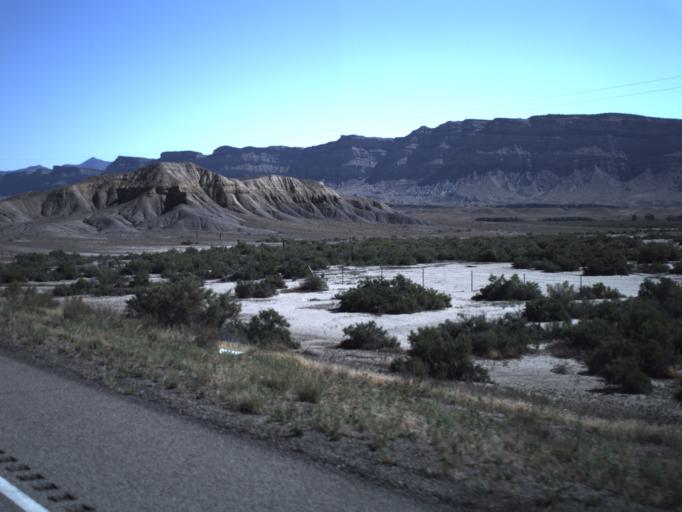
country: US
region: Utah
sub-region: Carbon County
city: East Carbon City
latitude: 39.2464
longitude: -110.3389
